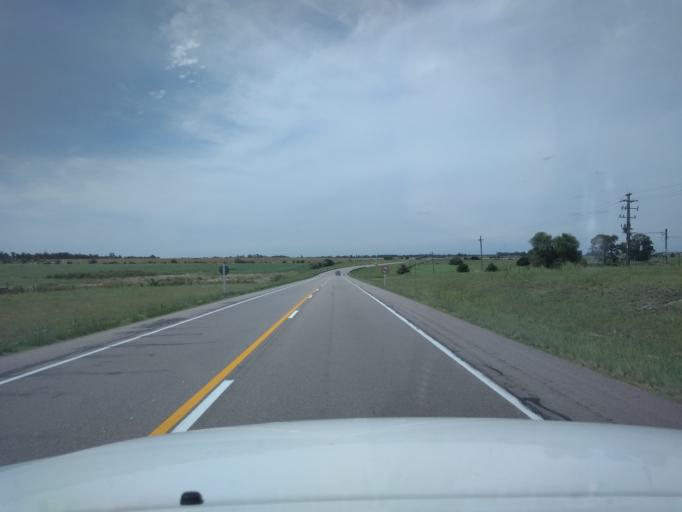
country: UY
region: Florida
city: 25 de Mayo
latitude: -34.2345
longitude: -56.2131
